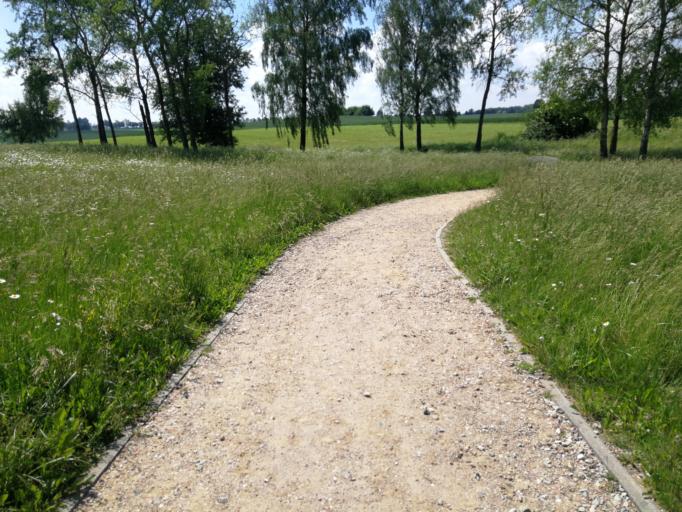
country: PL
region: Warmian-Masurian Voivodeship
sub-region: Powiat ostrodzki
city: Gierzwald
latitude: 53.4852
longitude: 20.1241
